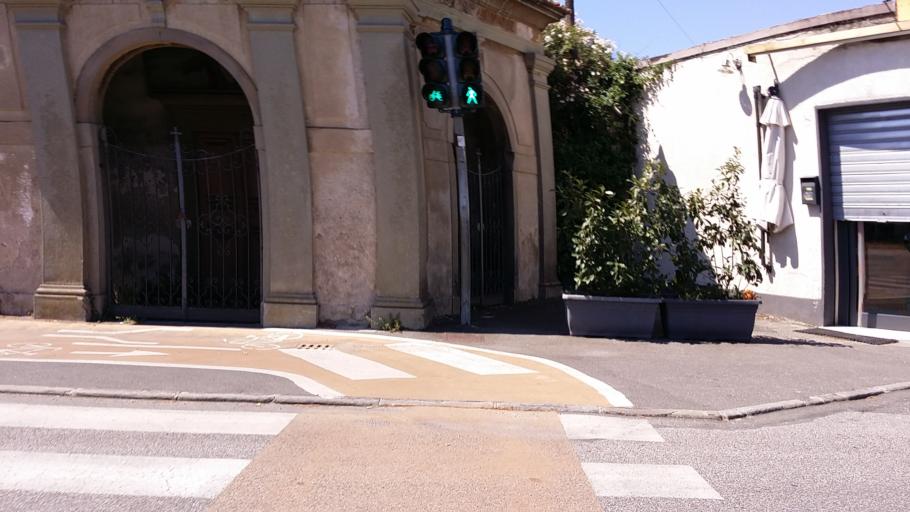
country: IT
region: Tuscany
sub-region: Provincia di Livorno
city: Livorno
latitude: 43.5324
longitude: 10.3194
